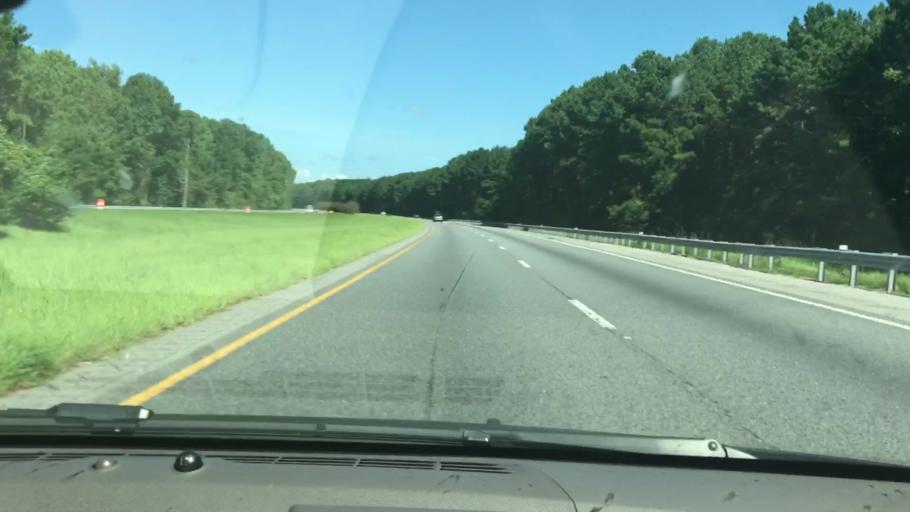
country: US
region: Alabama
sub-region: Russell County
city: Phenix City
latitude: 32.6184
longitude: -84.9515
